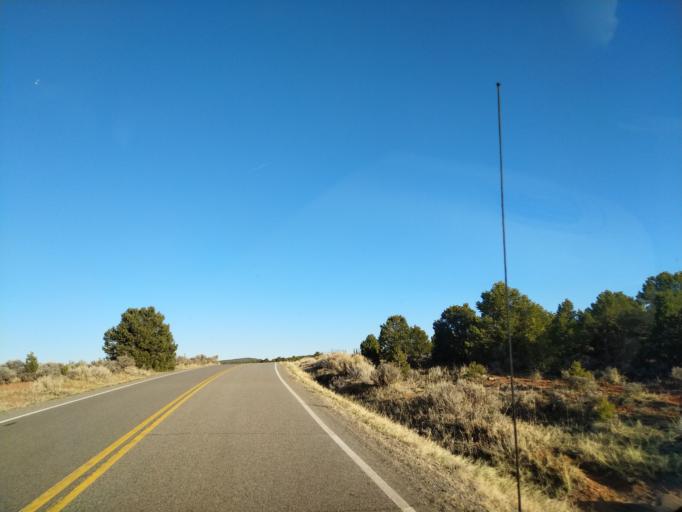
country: US
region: Colorado
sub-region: Mesa County
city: Redlands
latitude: 38.9914
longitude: -108.7678
